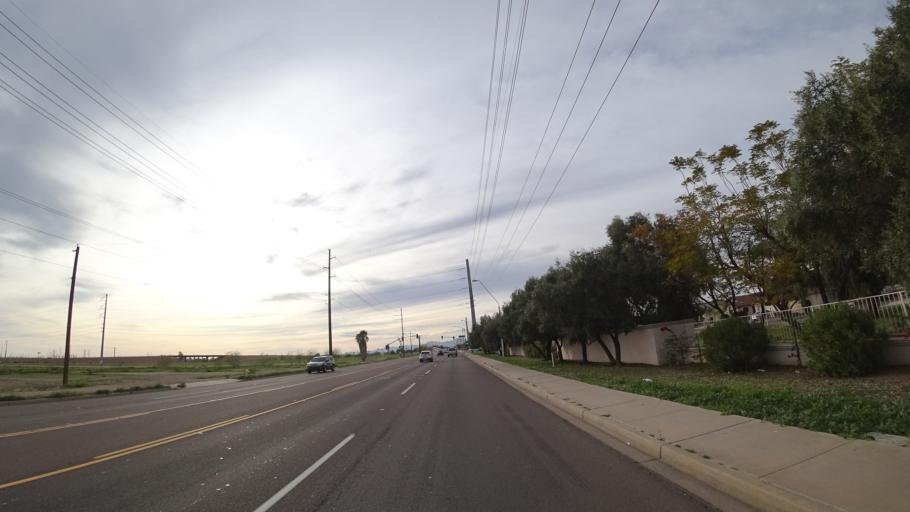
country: US
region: Arizona
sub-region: Maricopa County
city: Peoria
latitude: 33.5671
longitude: -112.2102
